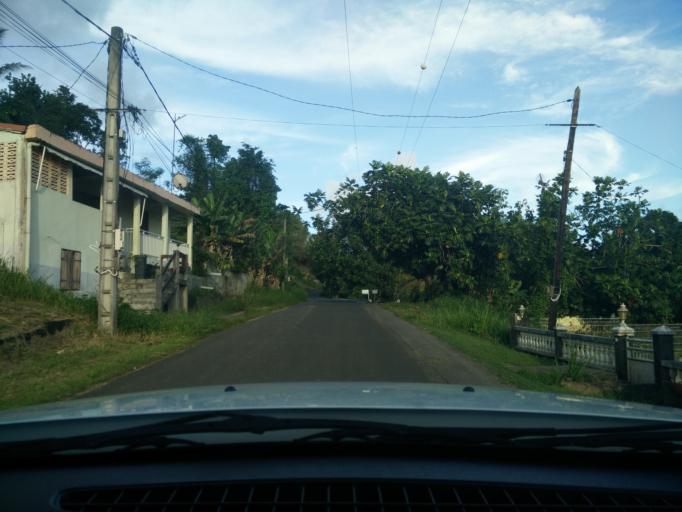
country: GP
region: Guadeloupe
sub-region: Guadeloupe
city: Les Abymes
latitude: 16.2500
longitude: -61.4973
